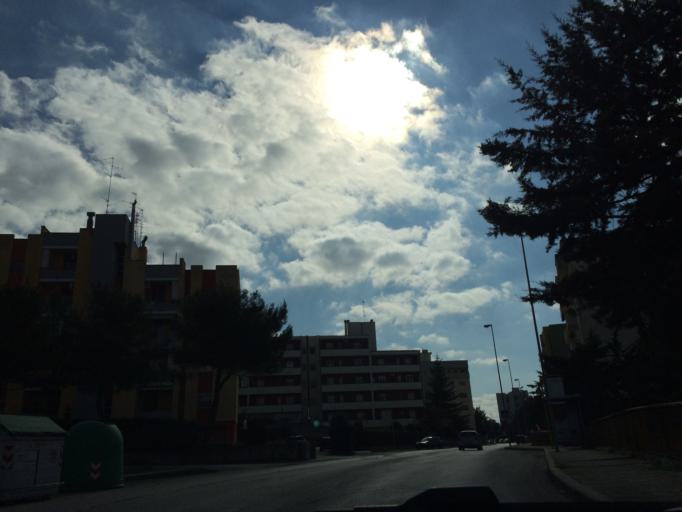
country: IT
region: Basilicate
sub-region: Provincia di Matera
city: Matera
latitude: 40.6721
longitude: 16.5874
